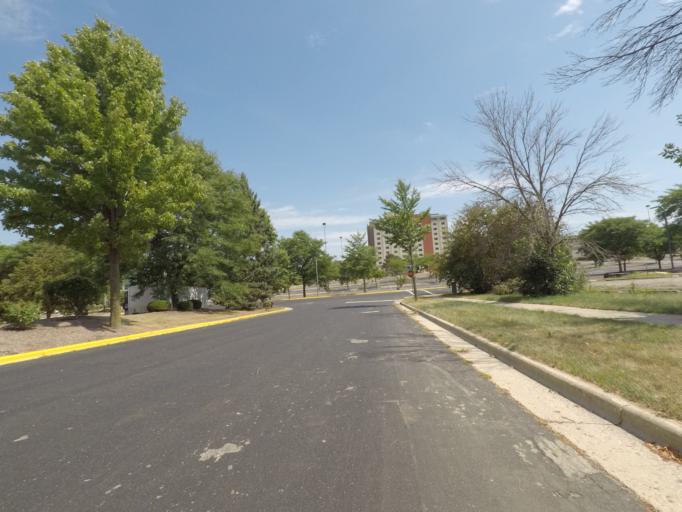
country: US
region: Wisconsin
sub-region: Dane County
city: Middleton
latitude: 43.0880
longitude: -89.5252
